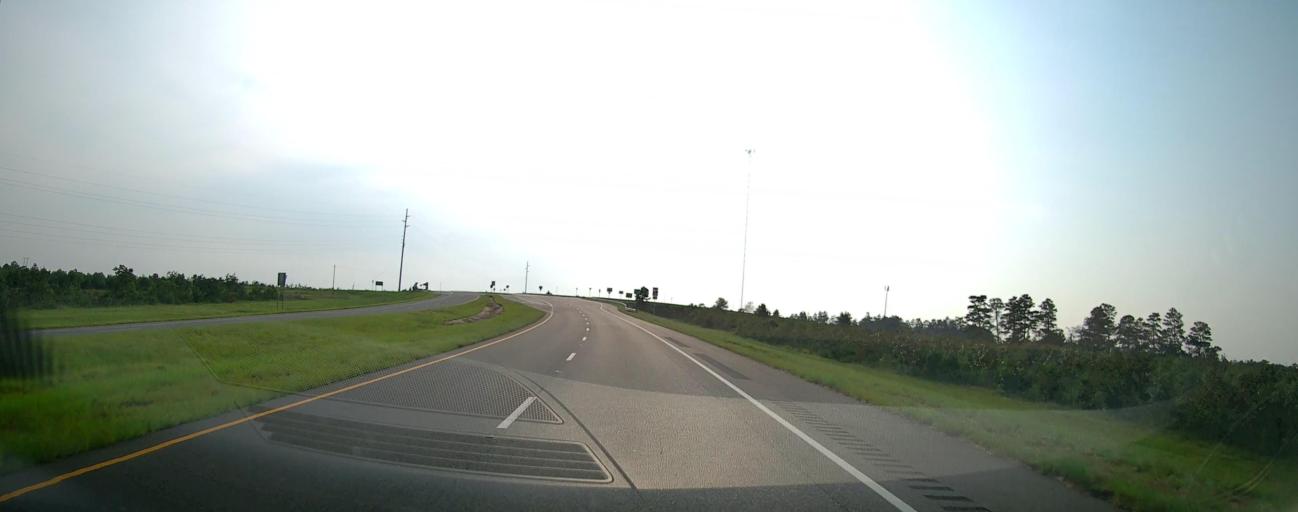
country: US
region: Georgia
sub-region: Talbot County
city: Talbotton
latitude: 32.5976
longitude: -84.4479
